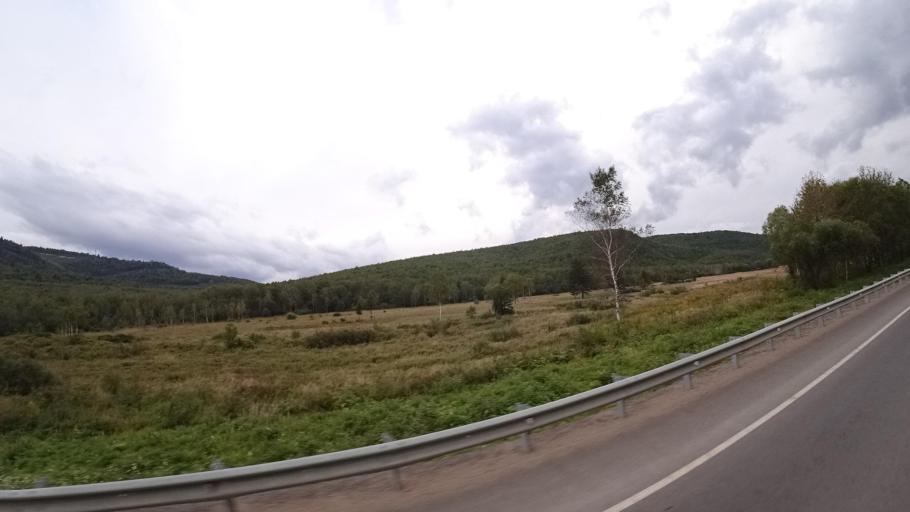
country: RU
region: Jewish Autonomous Oblast
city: Khingansk
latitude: 48.9837
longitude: 131.1468
